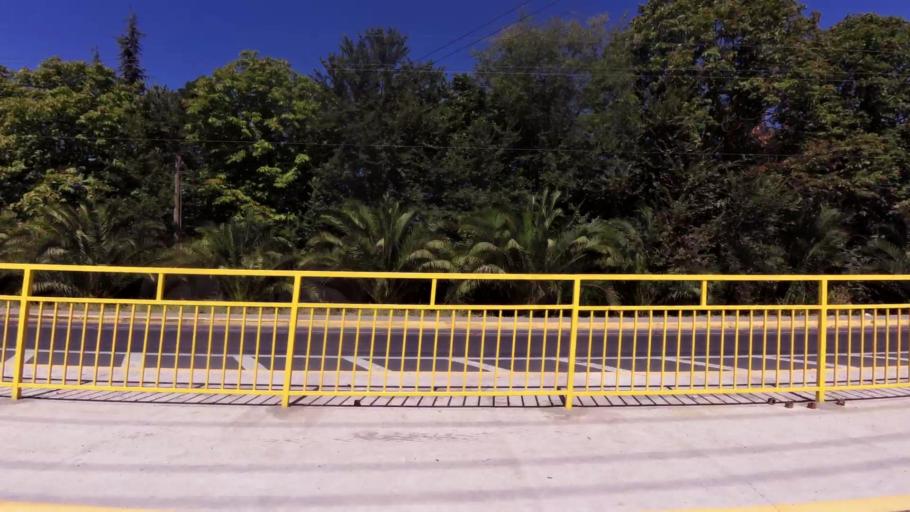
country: CL
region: Maule
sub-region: Provincia de Talca
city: Talca
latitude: -35.4328
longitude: -71.6083
